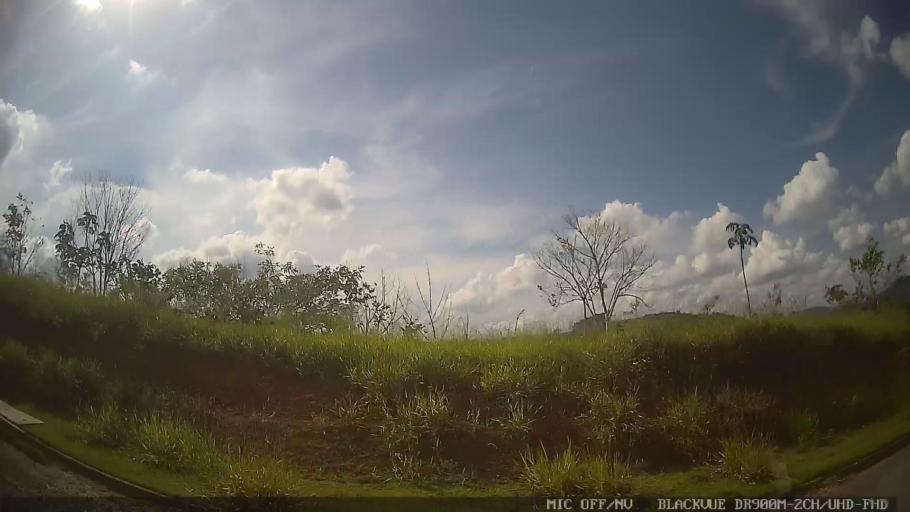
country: BR
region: Sao Paulo
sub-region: Atibaia
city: Atibaia
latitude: -23.0741
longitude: -46.5764
